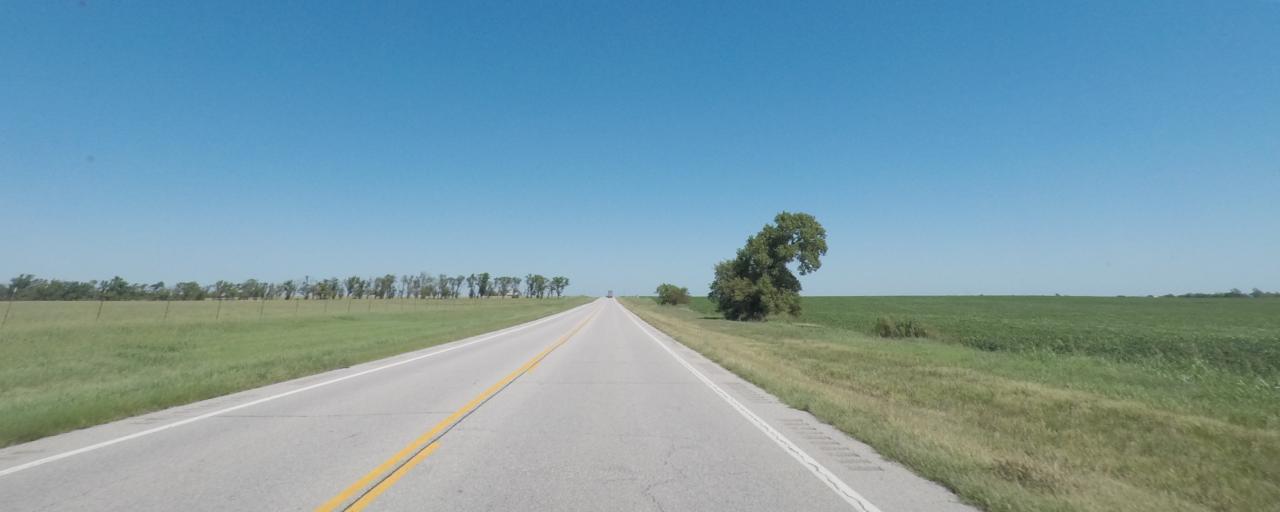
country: US
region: Kansas
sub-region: Sumner County
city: Wellington
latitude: 37.3543
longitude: -97.3848
